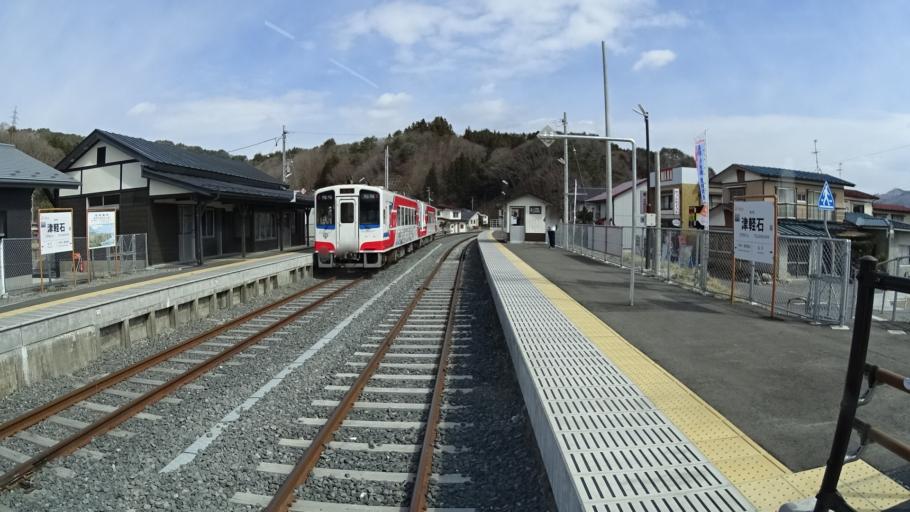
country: JP
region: Iwate
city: Miyako
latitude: 39.5813
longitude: 141.9377
